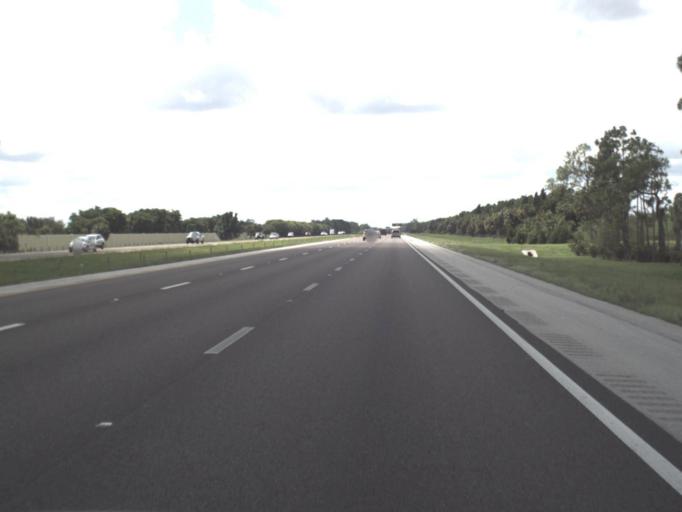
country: US
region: Florida
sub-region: Lee County
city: Bonita Springs
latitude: 26.3040
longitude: -81.7431
